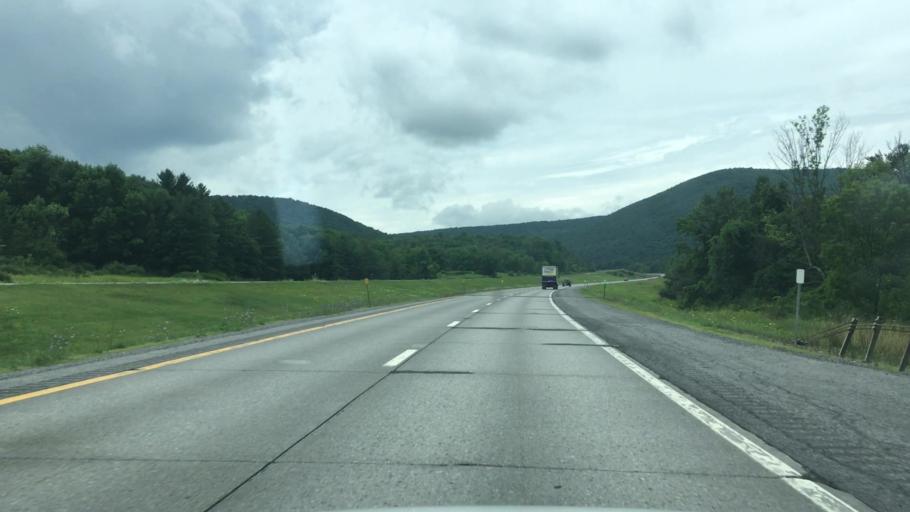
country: US
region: New York
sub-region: Schoharie County
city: Cobleskill
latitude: 42.6488
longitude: -74.6143
